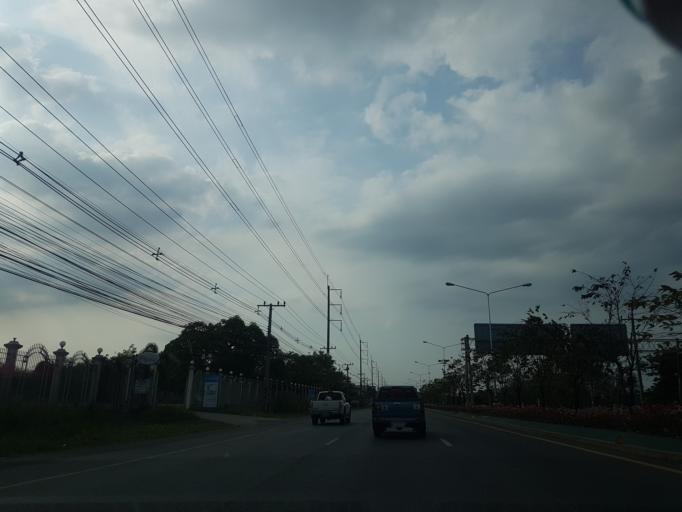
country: TH
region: Sara Buri
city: Phra Phutthabat
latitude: 14.7360
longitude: 100.7751
